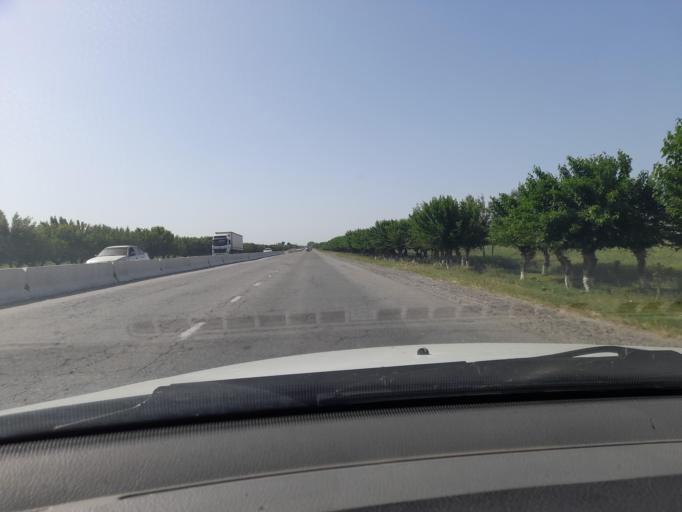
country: UZ
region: Samarqand
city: Daxbet
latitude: 39.8220
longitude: 66.8436
